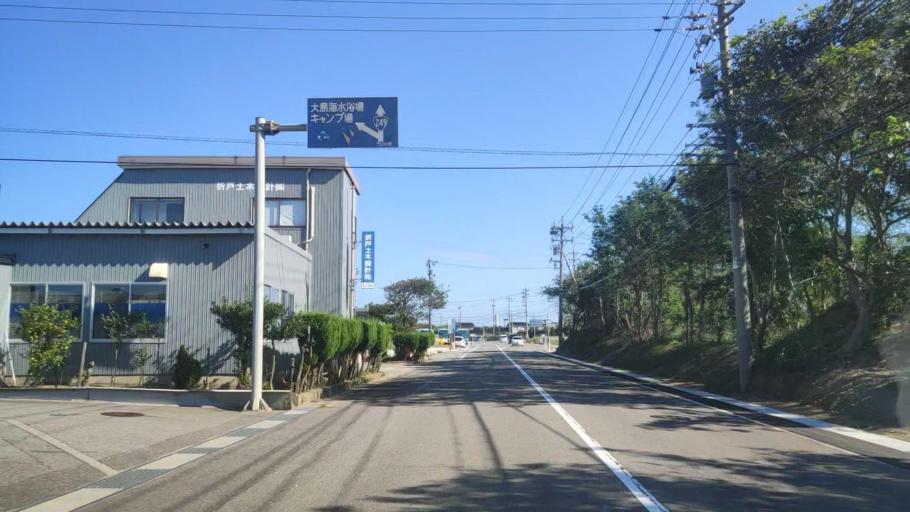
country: JP
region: Ishikawa
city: Hakui
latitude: 36.9770
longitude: 136.7761
